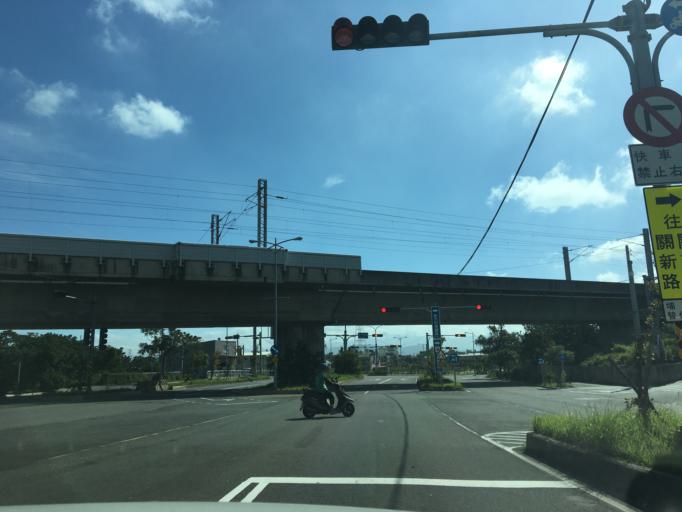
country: TW
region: Taiwan
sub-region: Hsinchu
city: Zhubei
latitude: 24.7944
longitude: 121.0198
